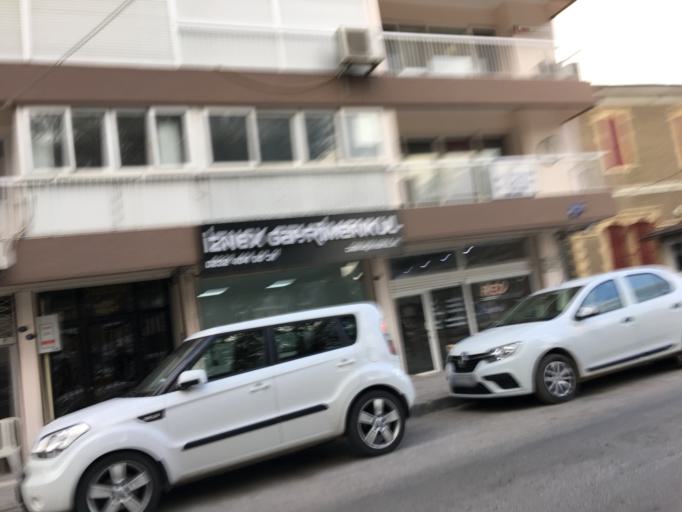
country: TR
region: Izmir
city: Izmir
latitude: 38.4367
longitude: 27.1467
